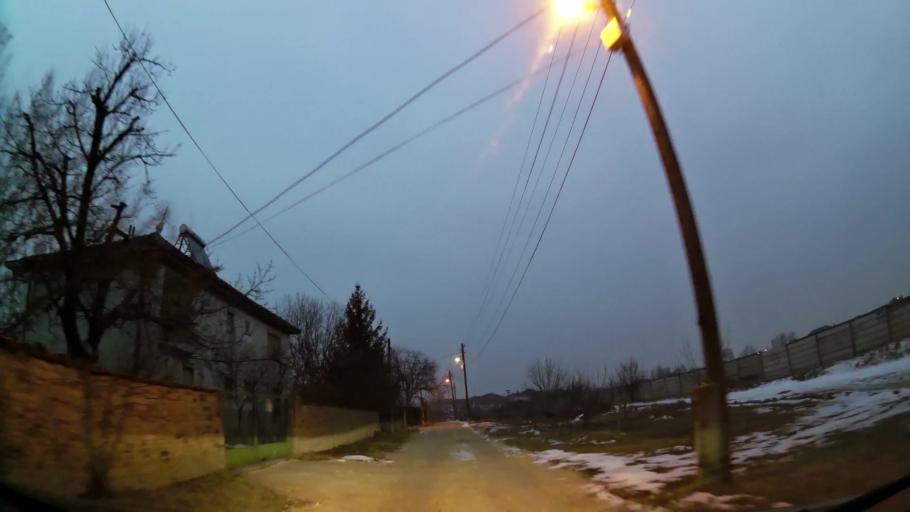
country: MK
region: Kisela Voda
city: Kisela Voda
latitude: 41.9693
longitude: 21.4903
